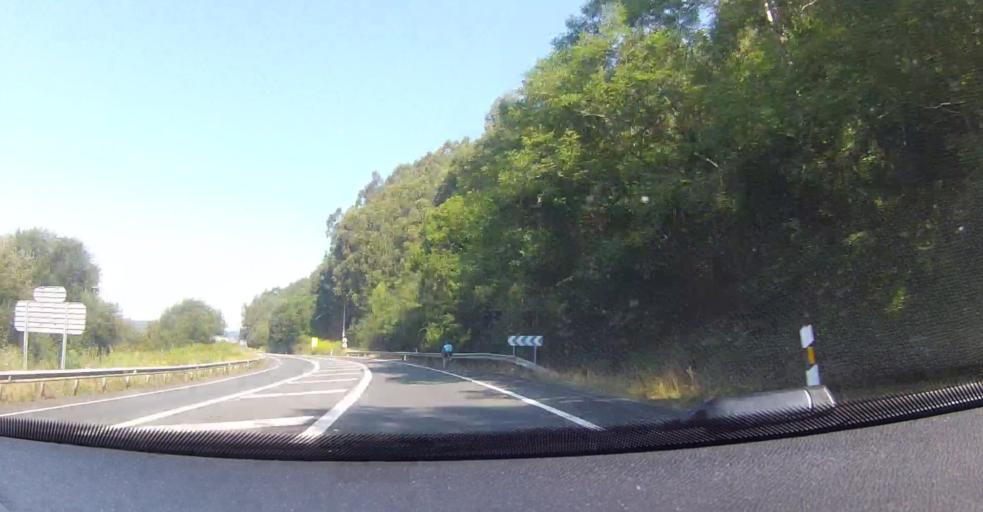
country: ES
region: Cantabria
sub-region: Provincia de Cantabria
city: Limpias
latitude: 43.3795
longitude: -3.4338
